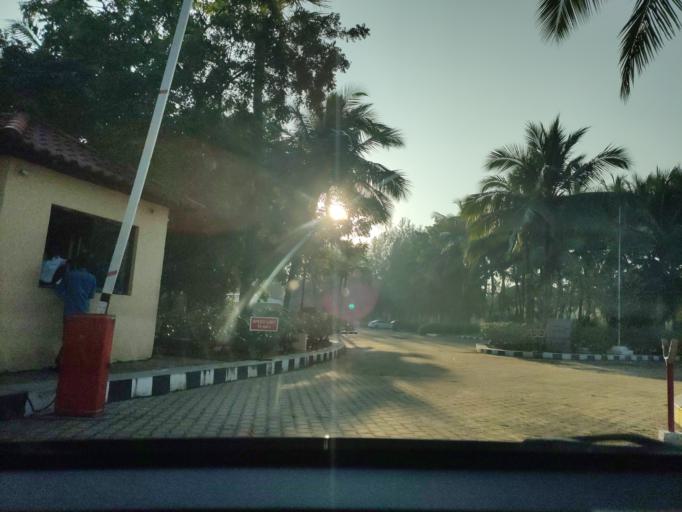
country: IN
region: Tamil Nadu
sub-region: Villupuram
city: Auroville
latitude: 12.0668
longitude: 79.8798
